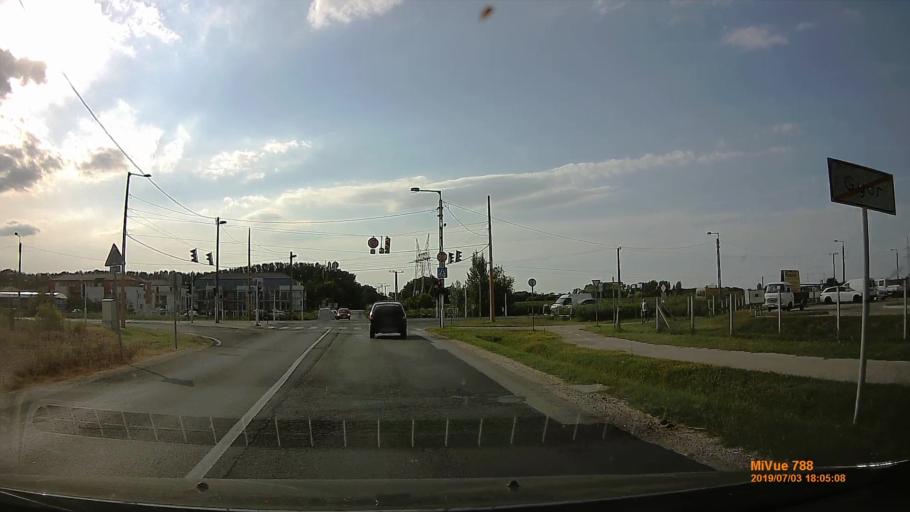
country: HU
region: Gyor-Moson-Sopron
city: Gyorujbarat
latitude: 47.6380
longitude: 17.6040
